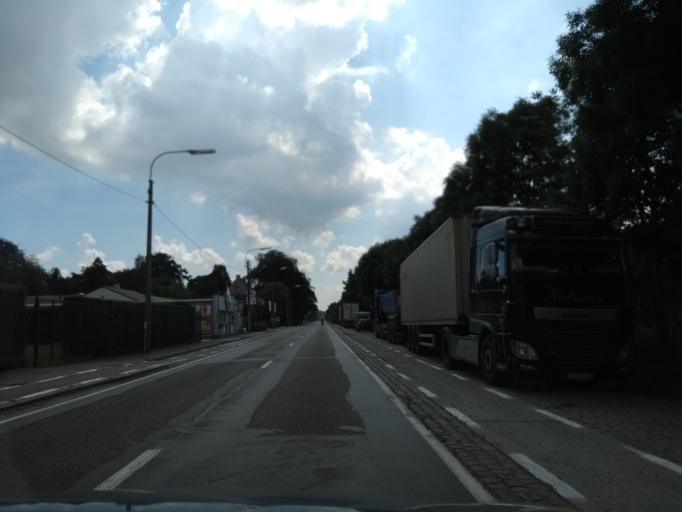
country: BE
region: Flanders
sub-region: Provincie Oost-Vlaanderen
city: Eeklo
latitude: 51.1803
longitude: 3.5519
